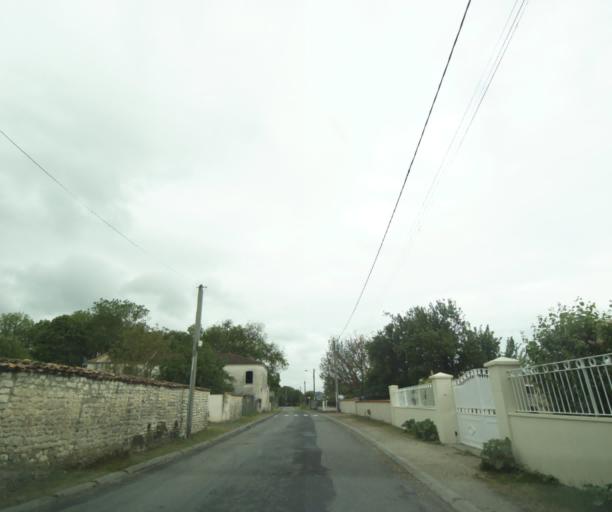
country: FR
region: Poitou-Charentes
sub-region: Departement de la Charente-Maritime
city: Chaniers
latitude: 45.6944
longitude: -0.5091
